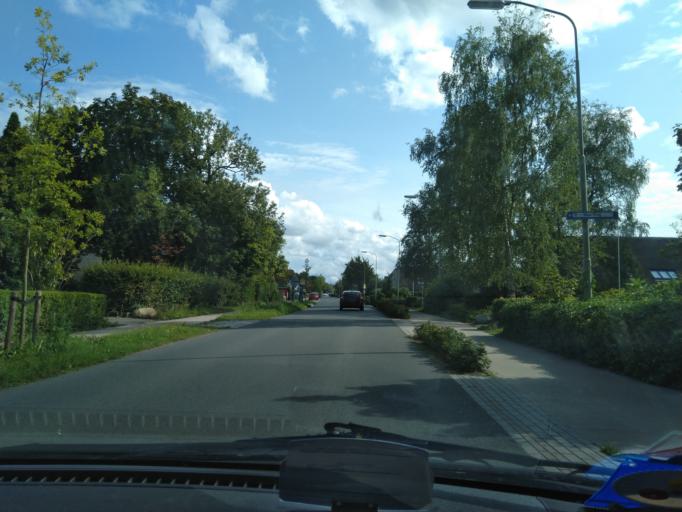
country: NL
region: Groningen
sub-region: Gemeente Groningen
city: Groningen
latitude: 53.1773
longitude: 6.5436
